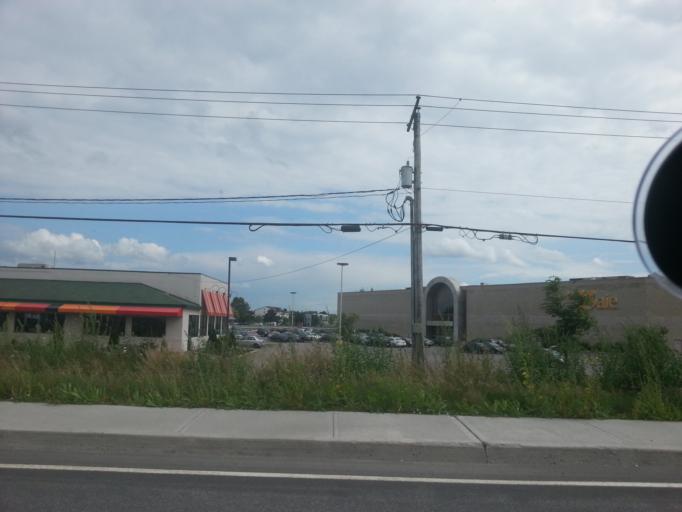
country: CA
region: Quebec
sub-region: Outaouais
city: Gatineau
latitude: 45.4784
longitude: -75.6937
